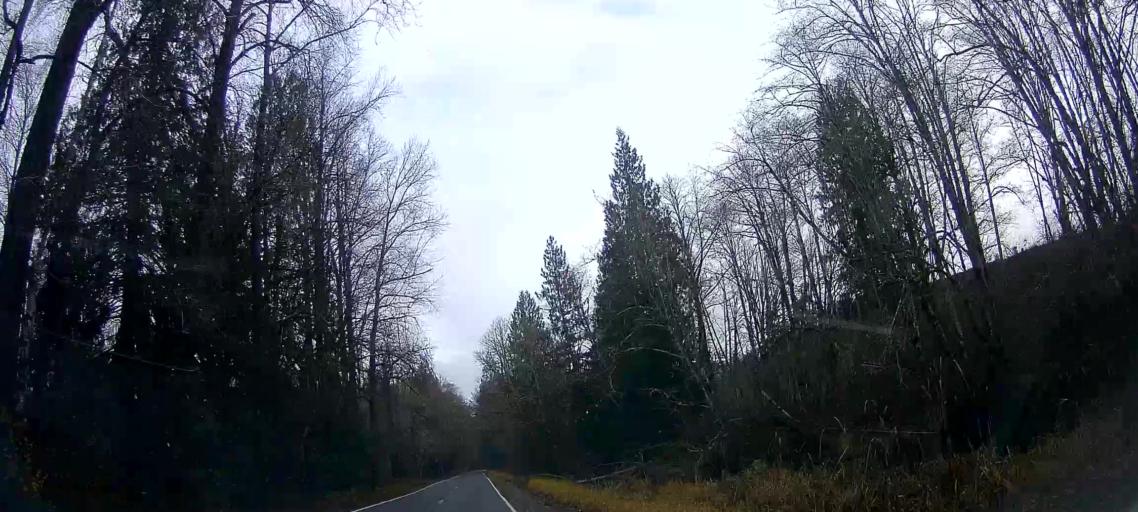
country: US
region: Washington
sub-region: Skagit County
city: Sedro-Woolley
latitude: 48.5157
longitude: -121.8703
